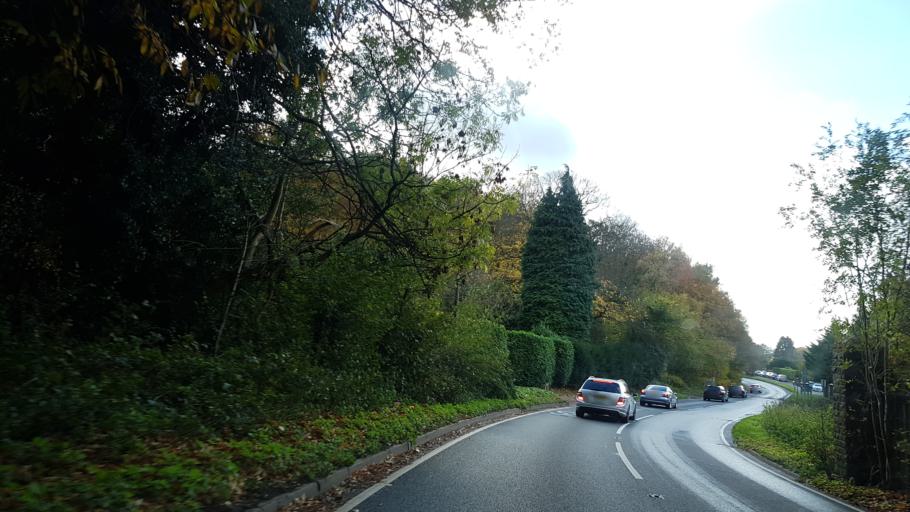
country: GB
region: England
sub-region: Surrey
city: Milford
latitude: 51.1381
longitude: -0.6726
